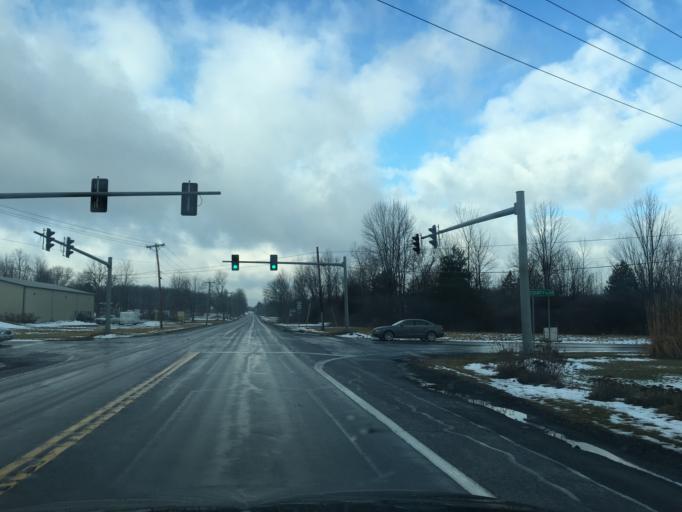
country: US
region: New York
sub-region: Ontario County
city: Manchester
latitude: 42.9670
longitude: -77.2766
